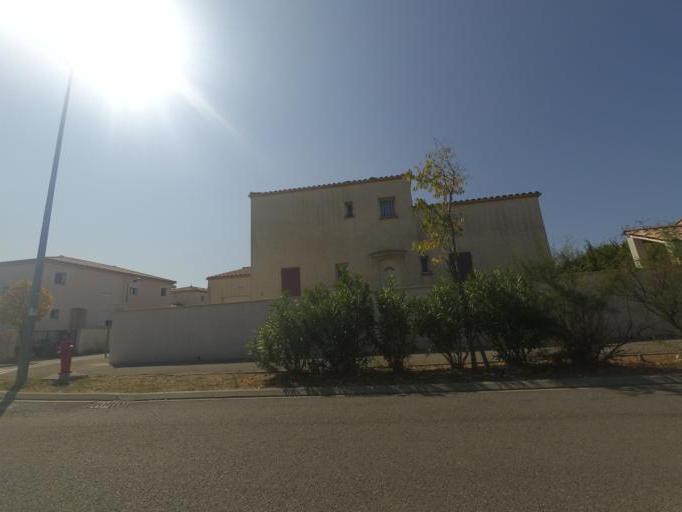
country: FR
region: Languedoc-Roussillon
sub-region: Departement du Gard
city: Calvisson
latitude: 43.7858
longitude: 4.1987
